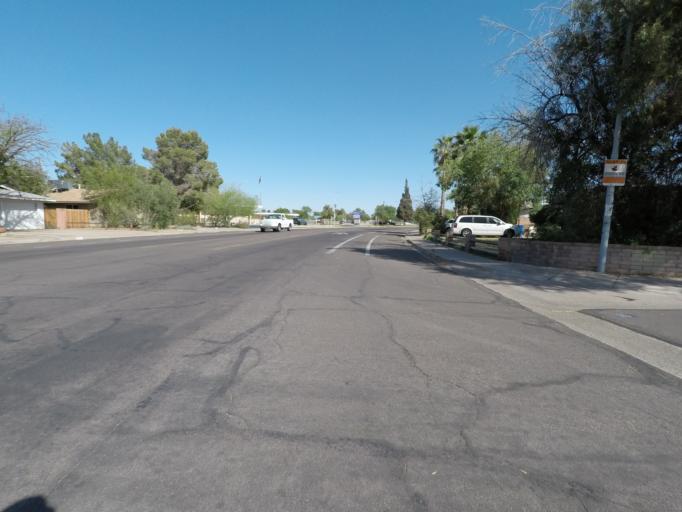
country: US
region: Arizona
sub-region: Maricopa County
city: Tempe
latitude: 33.4022
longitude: -111.9162
